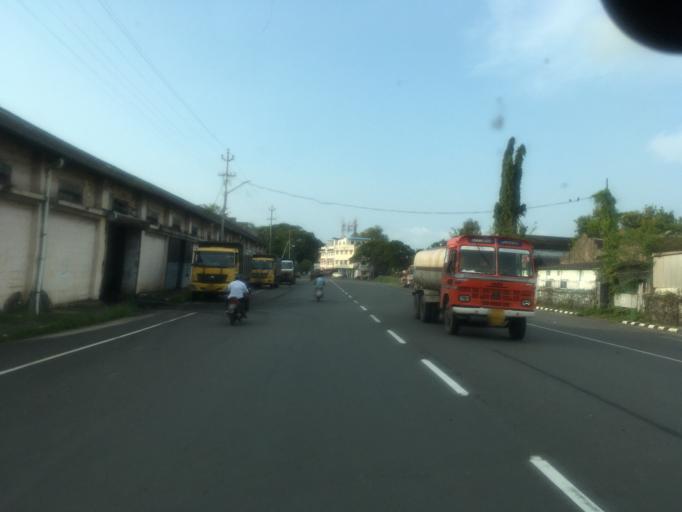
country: IN
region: Kerala
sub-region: Ernakulam
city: Cochin
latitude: 9.9609
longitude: 76.2670
